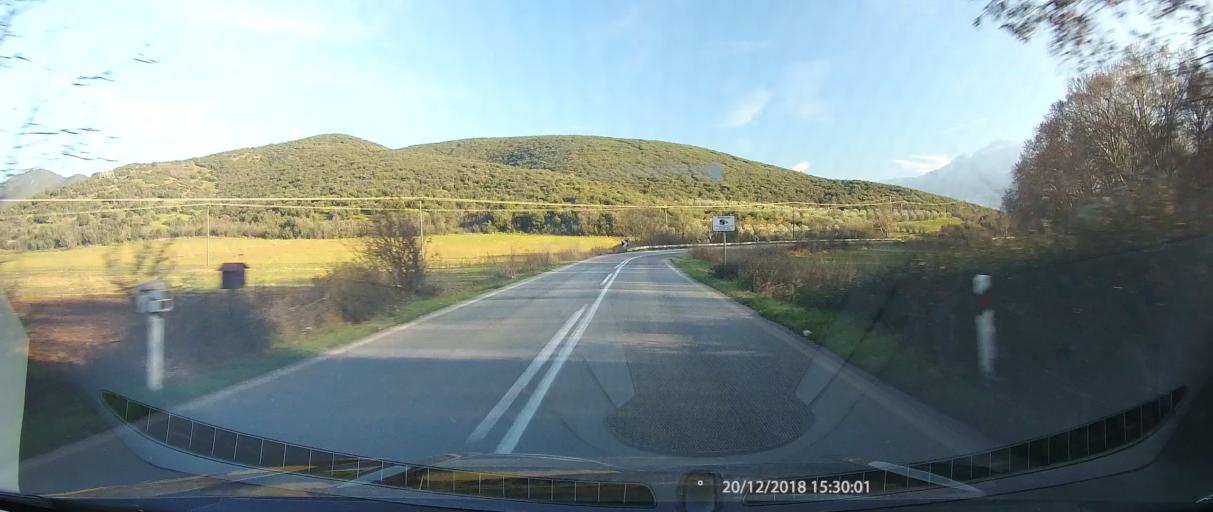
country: GR
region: Central Greece
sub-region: Nomos Fthiotidos
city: Lianokladhion
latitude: 38.9409
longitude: 22.2198
